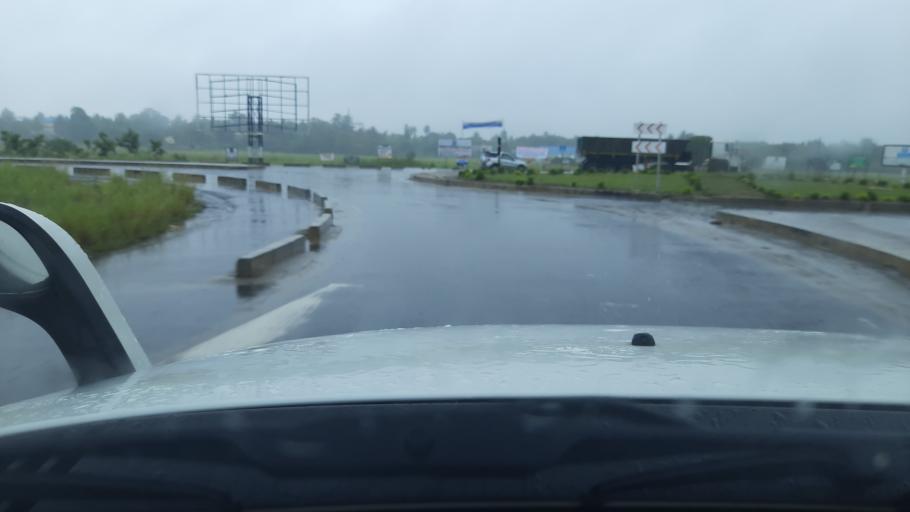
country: TZ
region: Pwani
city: Bagamoyo
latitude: -6.4578
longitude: 38.9075
